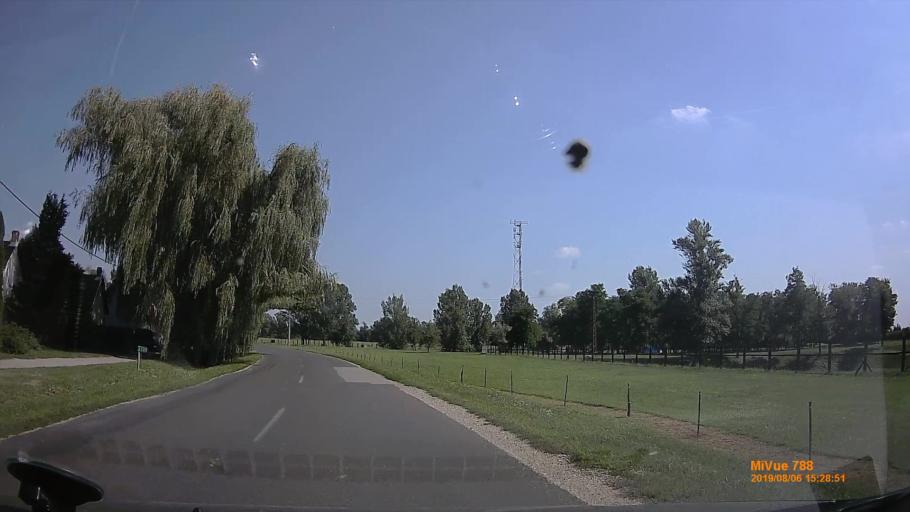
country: HR
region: Koprivnicko-Krizevacka
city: Sigetec
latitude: 46.2430
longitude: 16.9763
